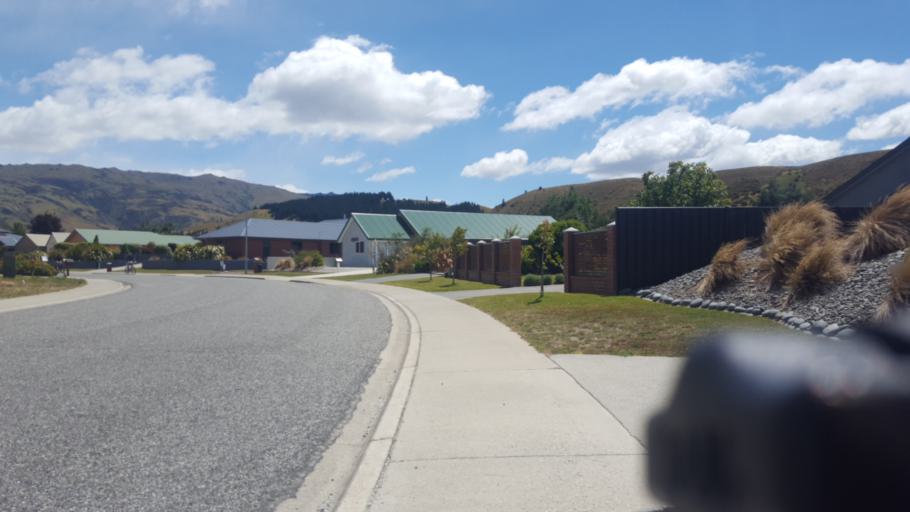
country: NZ
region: Otago
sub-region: Queenstown-Lakes District
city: Wanaka
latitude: -45.1945
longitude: 169.3336
